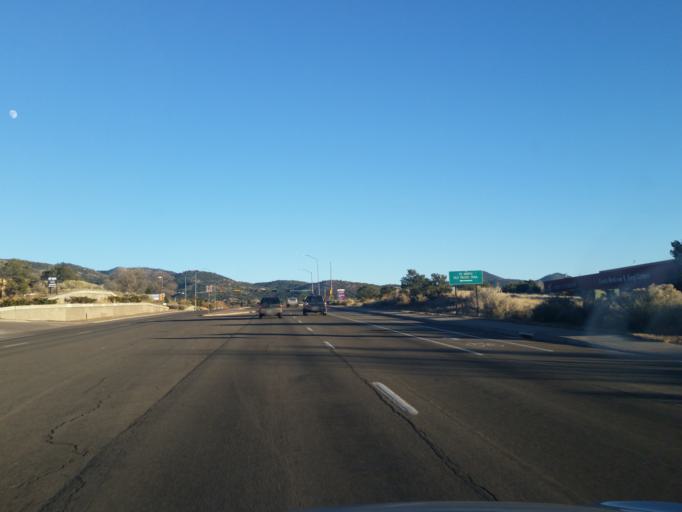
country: US
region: New Mexico
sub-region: Santa Fe County
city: Santa Fe
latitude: 35.6566
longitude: -105.9437
